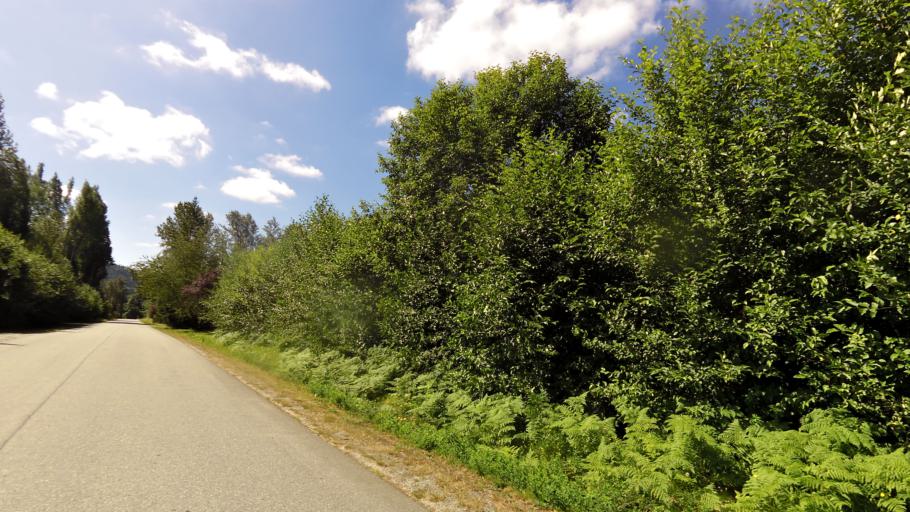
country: CA
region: British Columbia
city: Maple Ridge
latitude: 49.2198
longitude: -122.5237
